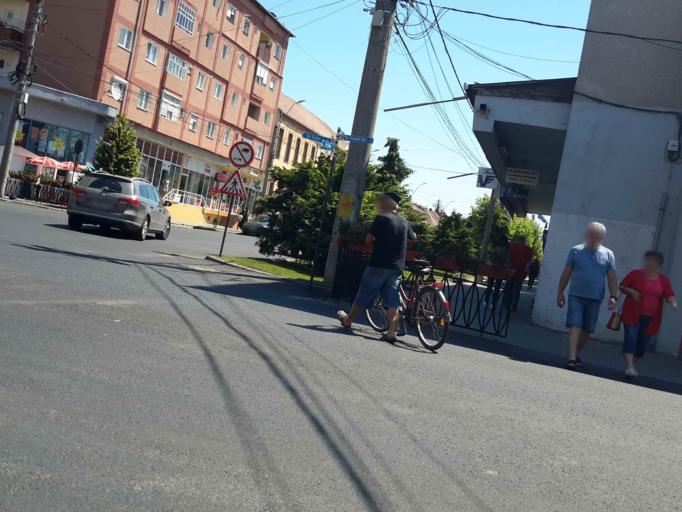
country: RO
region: Alba
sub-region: Municipiul Blaj
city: Blaj
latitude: 46.1768
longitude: 23.9168
